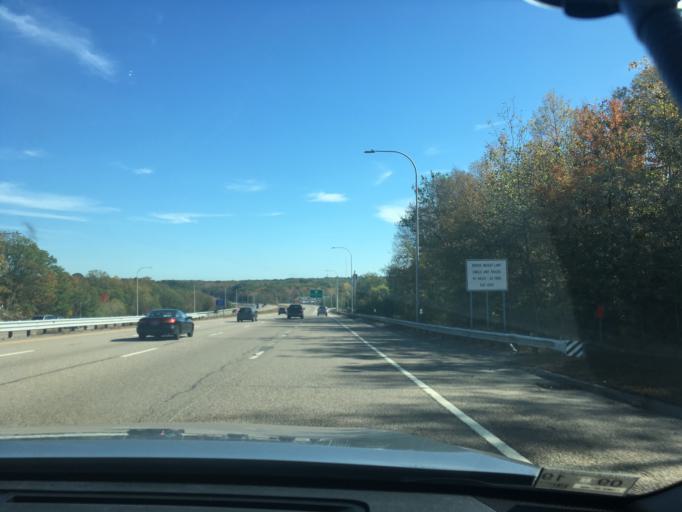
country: US
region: Rhode Island
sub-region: Providence County
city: Johnston
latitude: 41.8187
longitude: -71.5043
